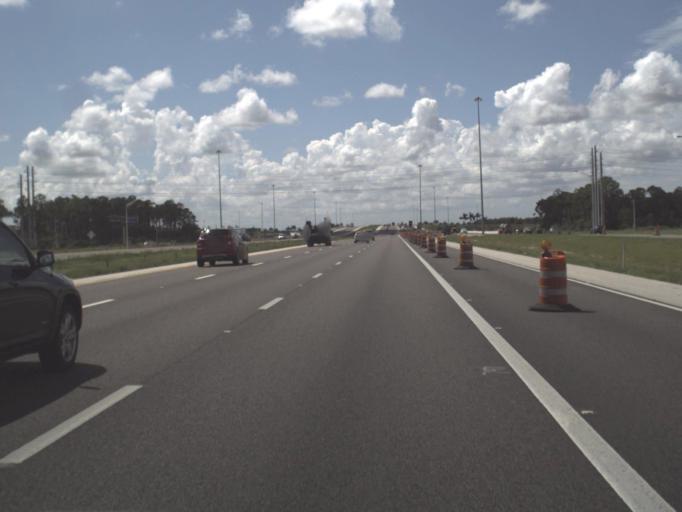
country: US
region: Florida
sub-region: Lee County
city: Three Oaks
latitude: 26.5029
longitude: -81.7947
